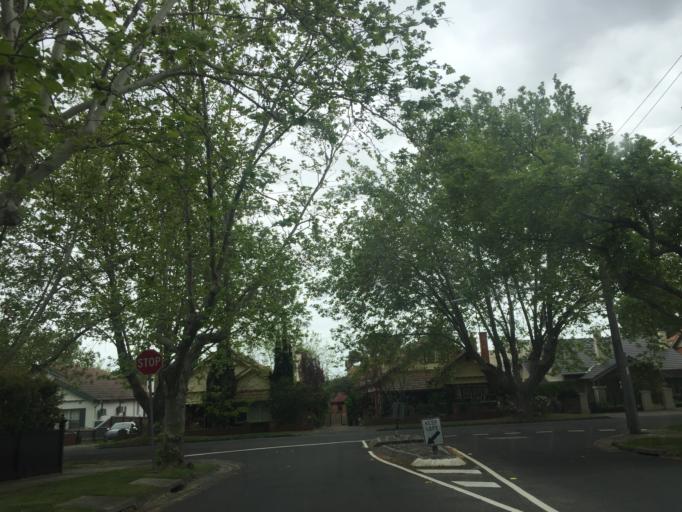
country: AU
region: Victoria
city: Balwyn
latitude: -37.8131
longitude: 145.0554
